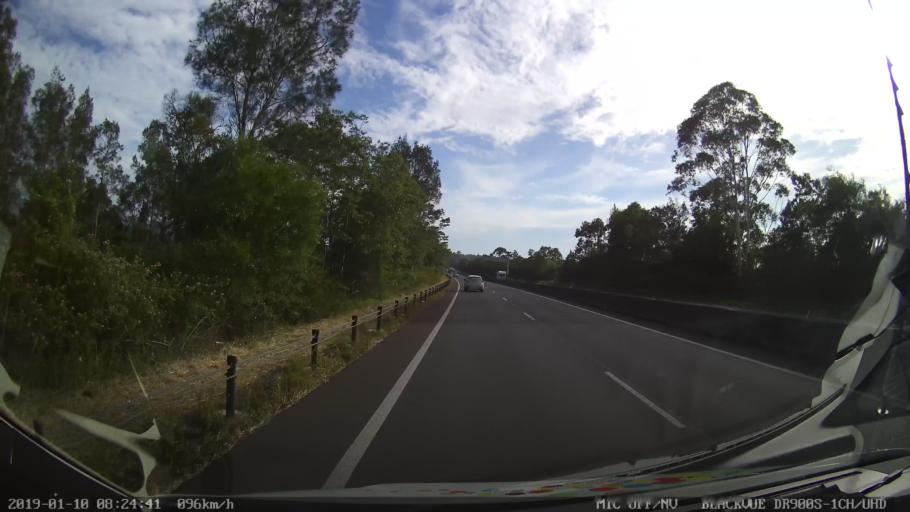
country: AU
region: New South Wales
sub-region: Coffs Harbour
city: Bonville
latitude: -30.4433
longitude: 153.0103
